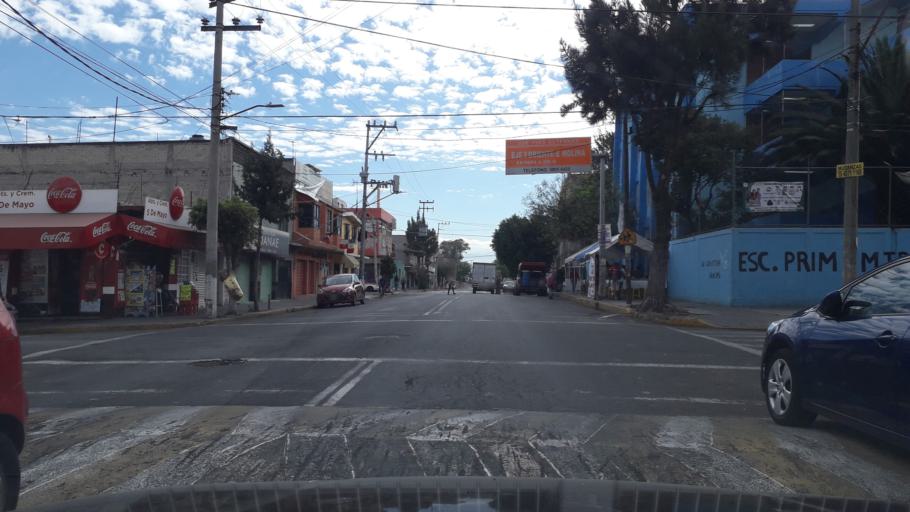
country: MX
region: Mexico City
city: Gustavo A. Madero
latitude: 19.4985
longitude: -99.0926
